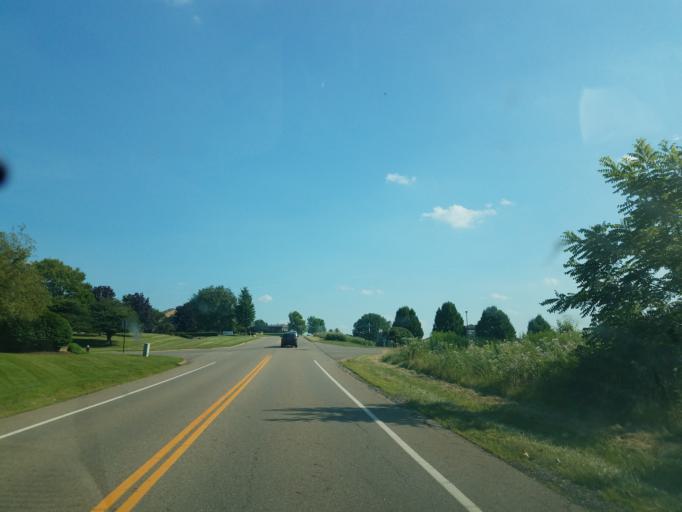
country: US
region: Ohio
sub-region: Stark County
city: Greentown
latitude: 40.9153
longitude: -81.4226
